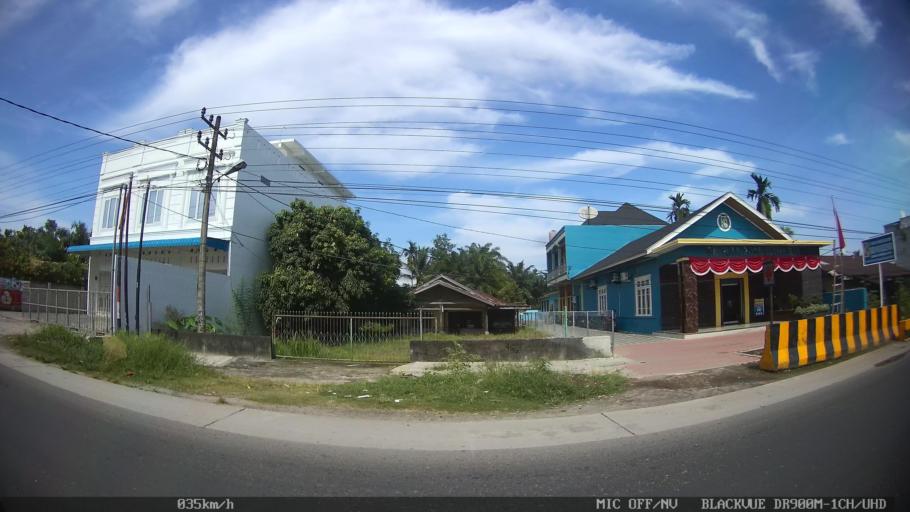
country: ID
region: North Sumatra
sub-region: Kabupaten Langkat
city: Stabat
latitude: 3.6935
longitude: 98.5072
